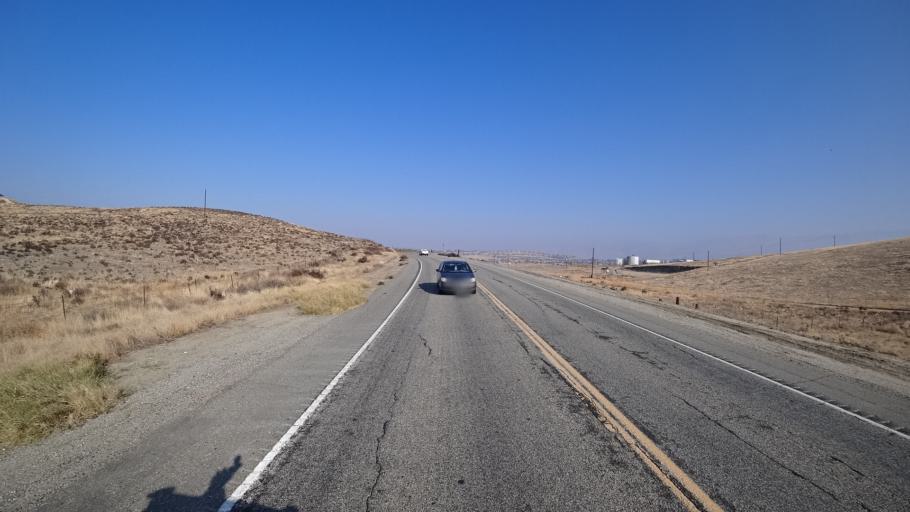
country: US
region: California
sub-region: Kern County
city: Lamont
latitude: 35.3979
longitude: -118.8568
